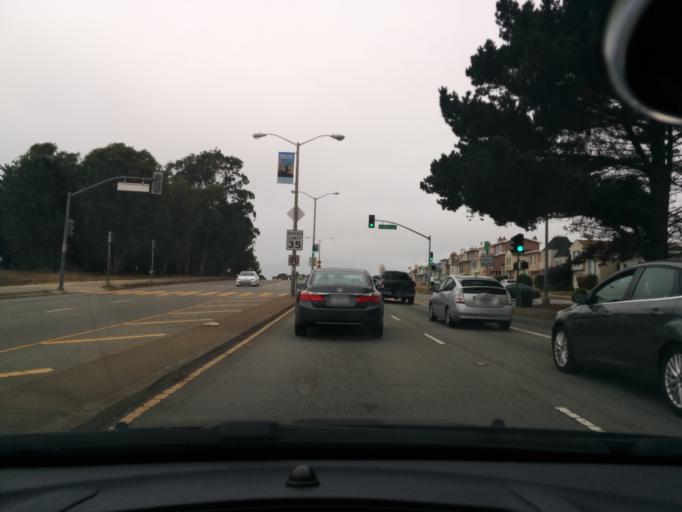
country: US
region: California
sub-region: San Mateo County
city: Daly City
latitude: 37.7295
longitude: -122.4861
